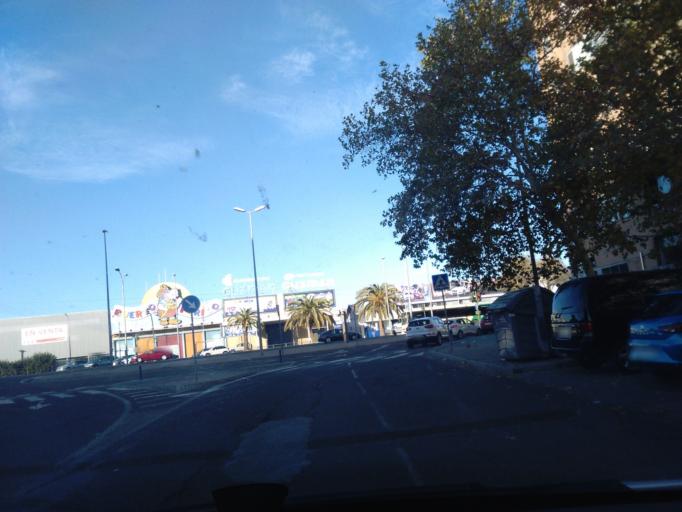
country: ES
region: Andalusia
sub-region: Provincia de Sevilla
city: Sevilla
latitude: 37.3859
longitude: -5.9435
